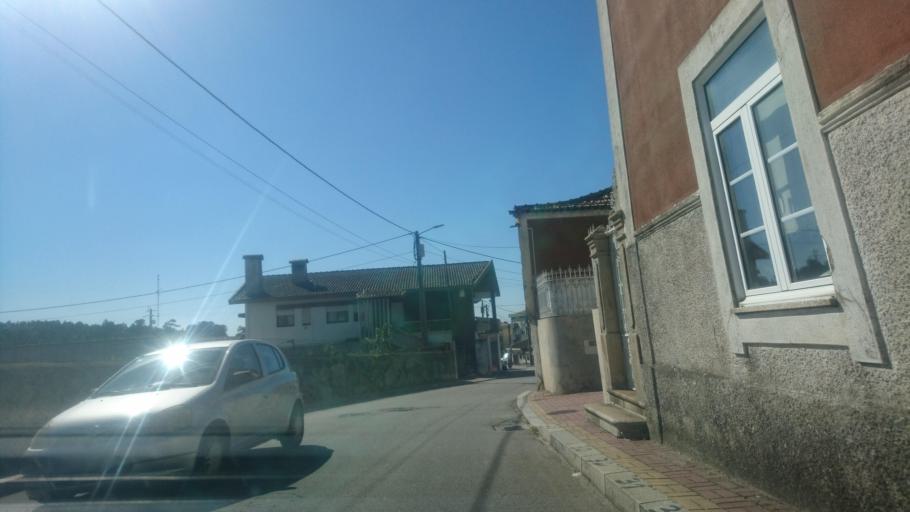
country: PT
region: Aveiro
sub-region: Santa Maria da Feira
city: Lamas
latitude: 40.9816
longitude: -8.5704
